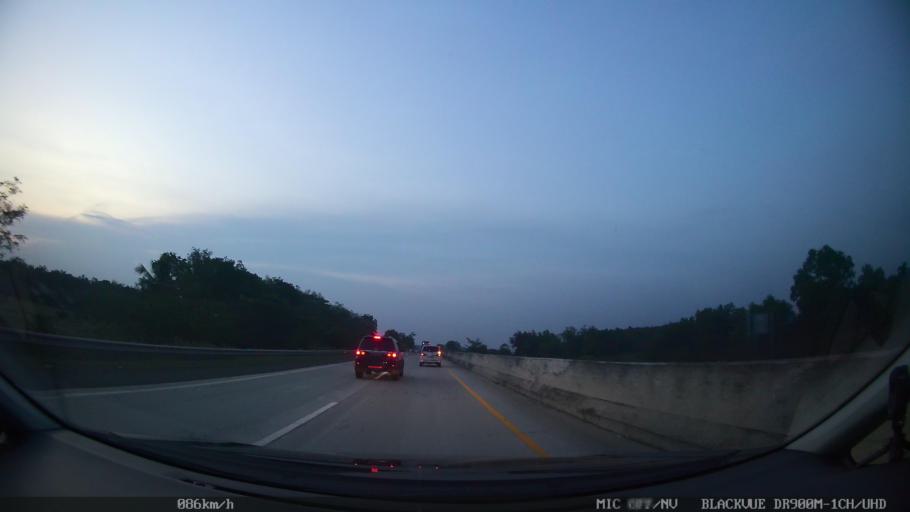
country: ID
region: Lampung
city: Sidorejo
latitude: -5.5967
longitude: 105.5509
